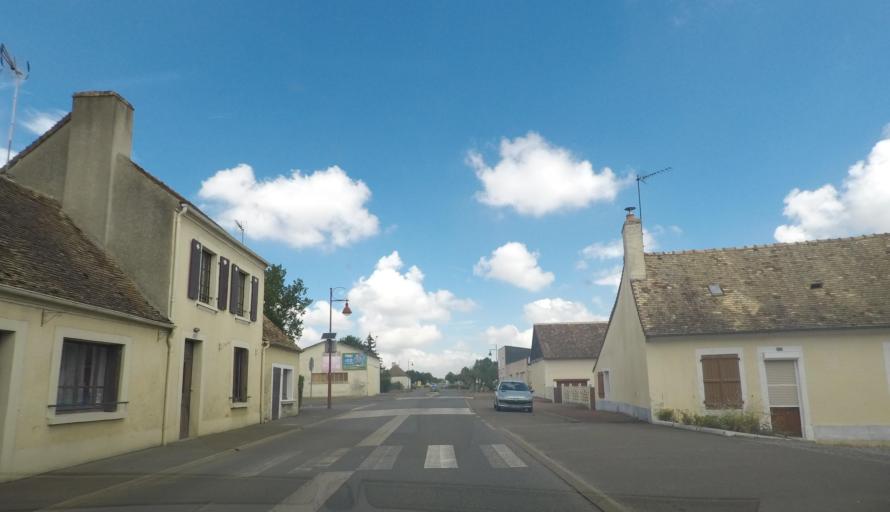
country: FR
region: Pays de la Loire
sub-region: Departement de la Sarthe
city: Bonnetable
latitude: 48.2278
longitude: 0.4306
